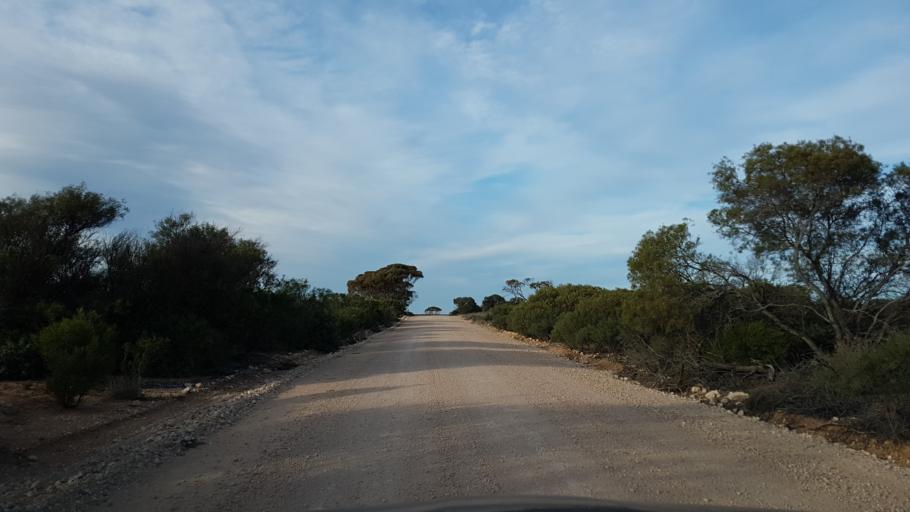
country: AU
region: South Australia
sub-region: Mid Murray
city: Mannum
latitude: -34.7498
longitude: 139.5740
